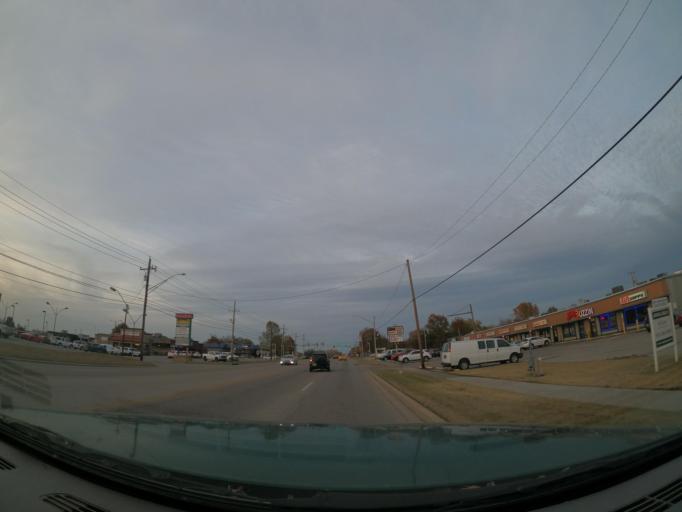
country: US
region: Oklahoma
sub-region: Tulsa County
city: Broken Arrow
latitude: 36.0307
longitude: -95.7974
